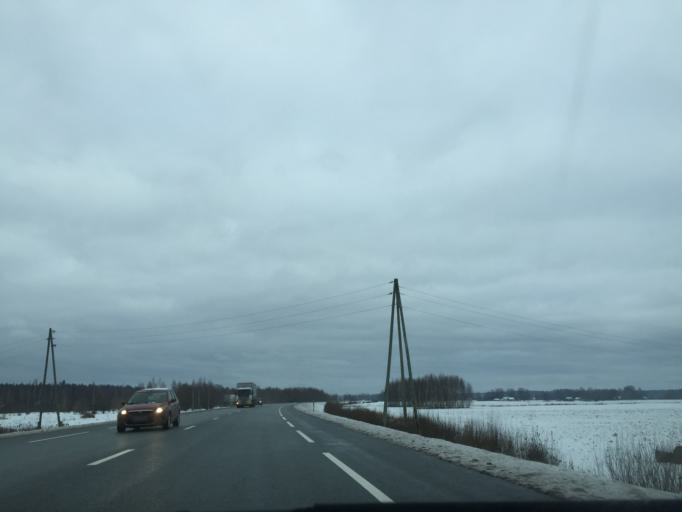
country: LV
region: Adazi
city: Adazi
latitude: 57.1141
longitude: 24.3225
